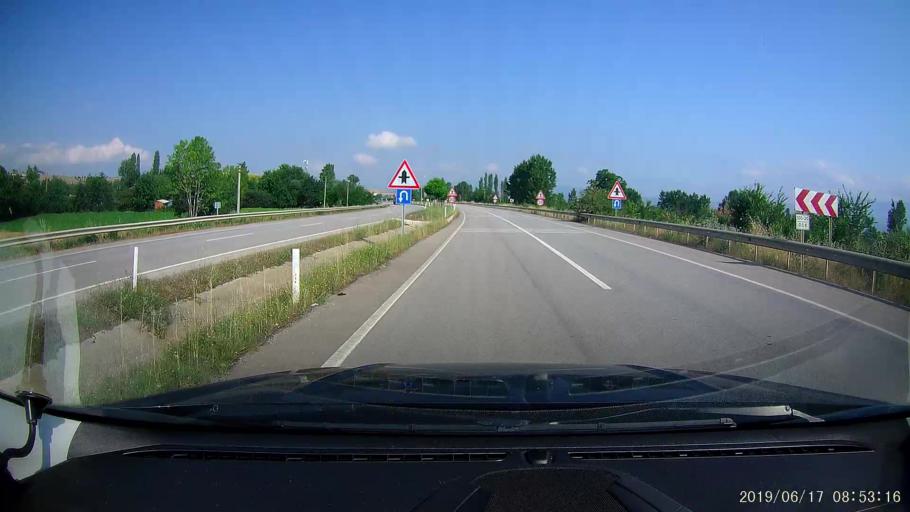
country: TR
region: Tokat
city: Erbaa
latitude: 40.7082
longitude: 36.4841
